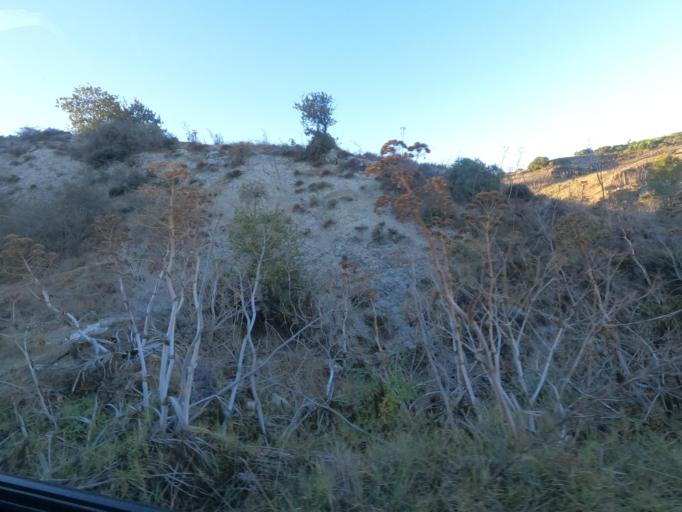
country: CY
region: Pafos
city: Mesogi
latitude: 34.7951
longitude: 32.4748
